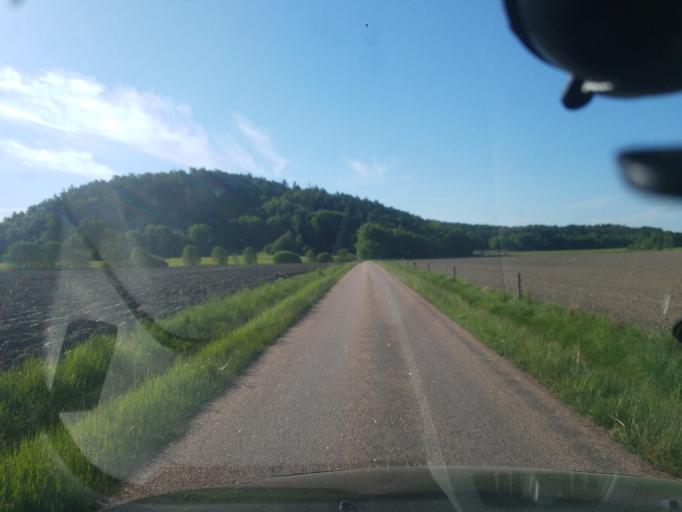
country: SE
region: Vaestra Goetaland
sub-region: Orust
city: Henan
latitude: 58.2891
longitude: 11.6378
